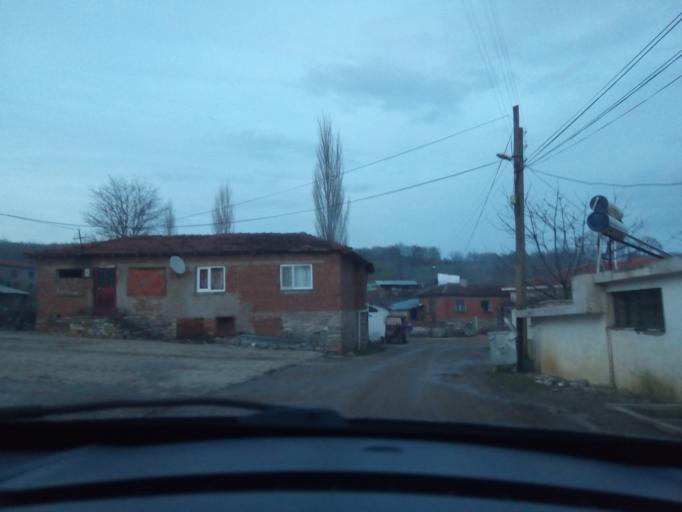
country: TR
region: Balikesir
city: Omerkoy
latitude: 39.9101
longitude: 28.0372
